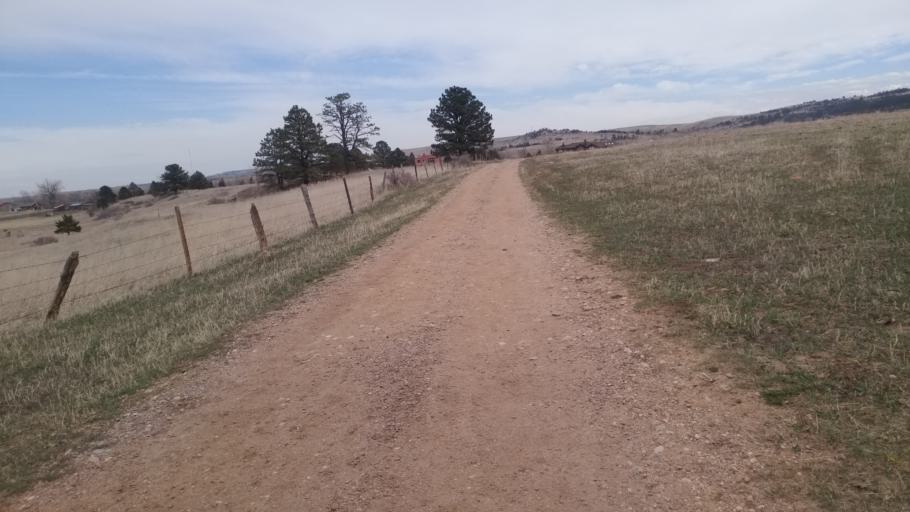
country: US
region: Colorado
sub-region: Boulder County
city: Boulder
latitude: 39.9605
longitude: -105.2457
